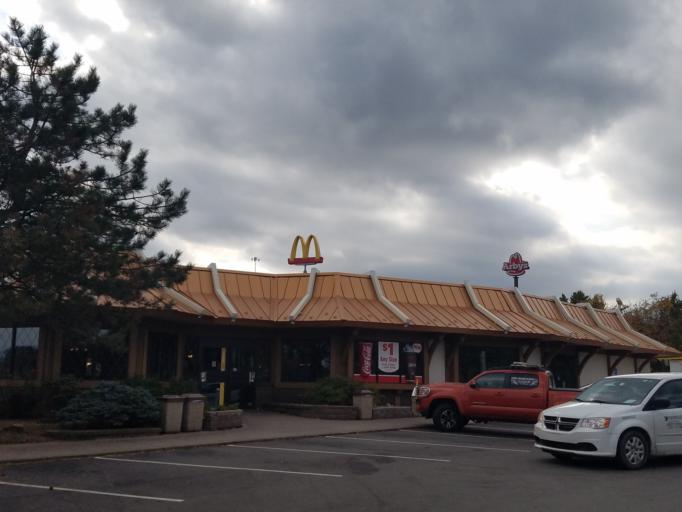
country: US
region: Ohio
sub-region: Richland County
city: Mansfield
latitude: 40.6982
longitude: -82.5117
